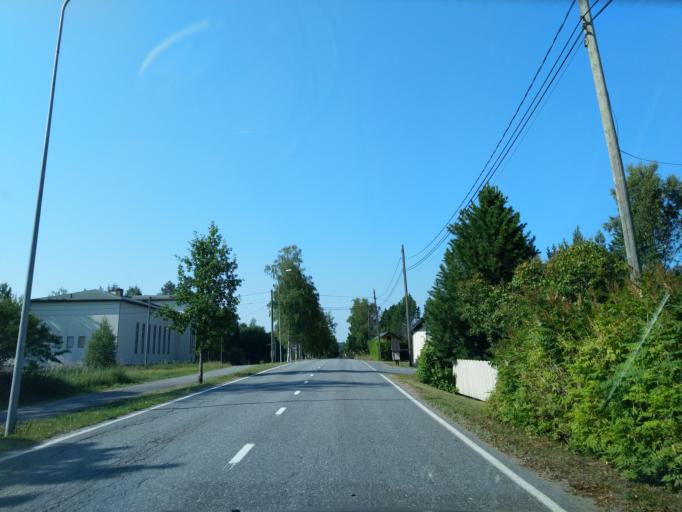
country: FI
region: Satakunta
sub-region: Pori
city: Pomarkku
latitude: 61.7014
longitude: 22.0192
